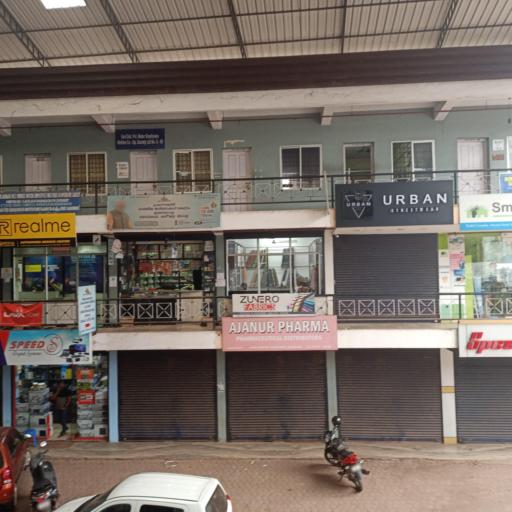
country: IN
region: Kerala
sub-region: Kasaragod District
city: Kasaragod
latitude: 12.5035
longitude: 74.9896
